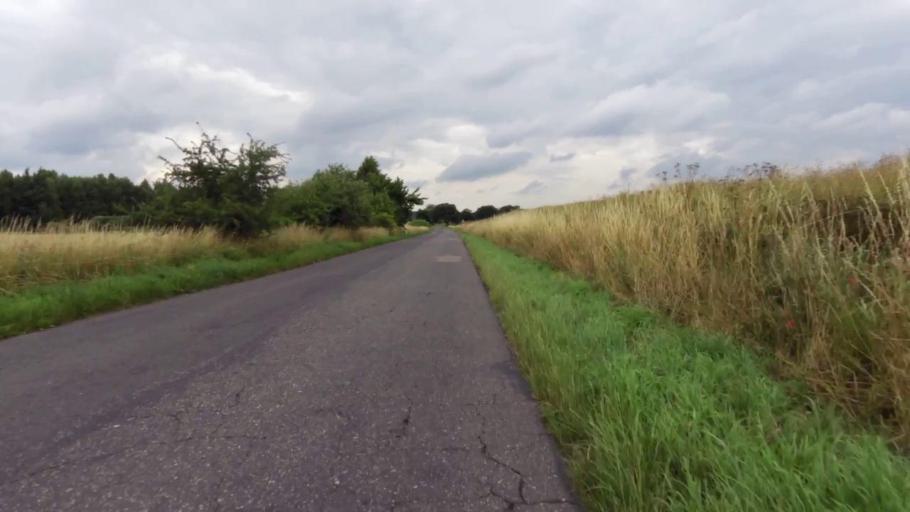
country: PL
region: West Pomeranian Voivodeship
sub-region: Powiat mysliborski
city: Mysliborz
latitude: 52.9588
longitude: 14.8829
